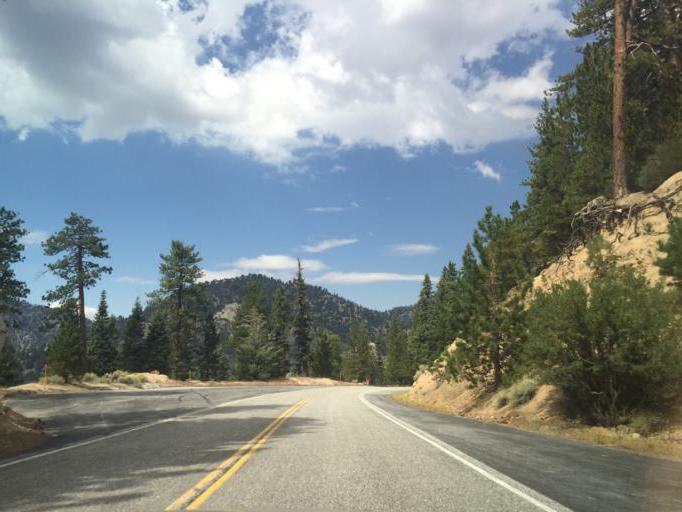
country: US
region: California
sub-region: Los Angeles County
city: Littlerock
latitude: 34.3519
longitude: -117.8807
